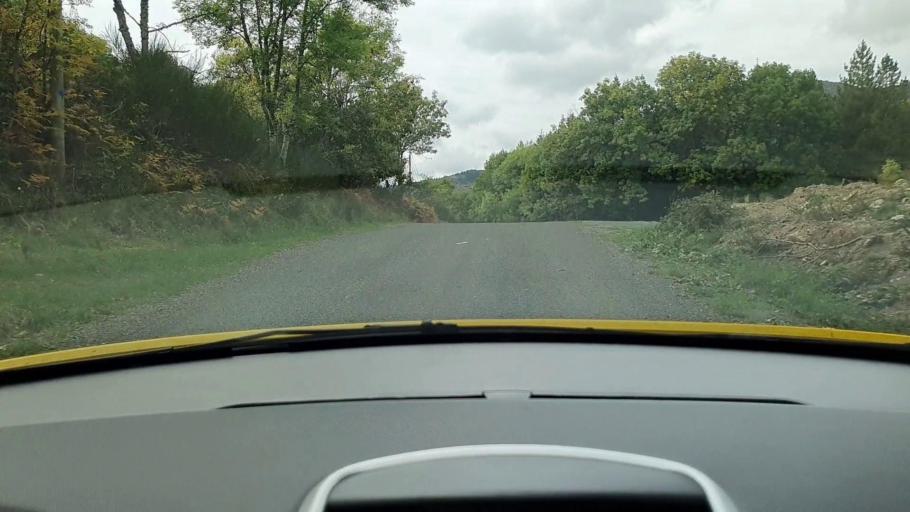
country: FR
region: Languedoc-Roussillon
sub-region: Departement de la Lozere
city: Meyrueis
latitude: 44.0647
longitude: 3.4372
